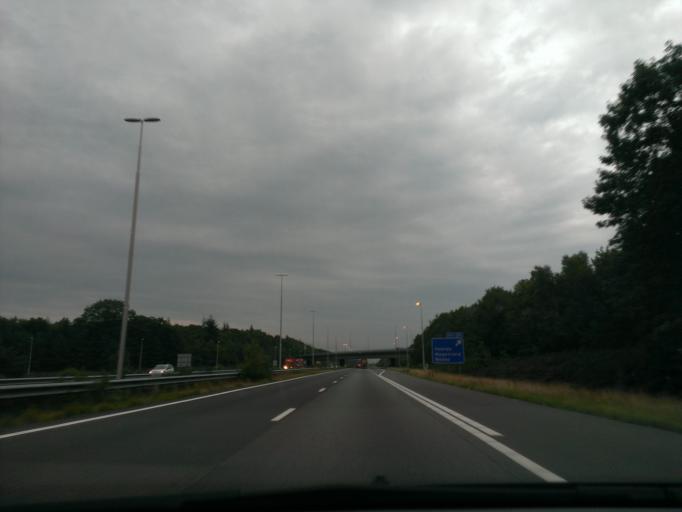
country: NL
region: Gelderland
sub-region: Gemeente Heerde
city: Heerde
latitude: 52.4098
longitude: 6.0156
